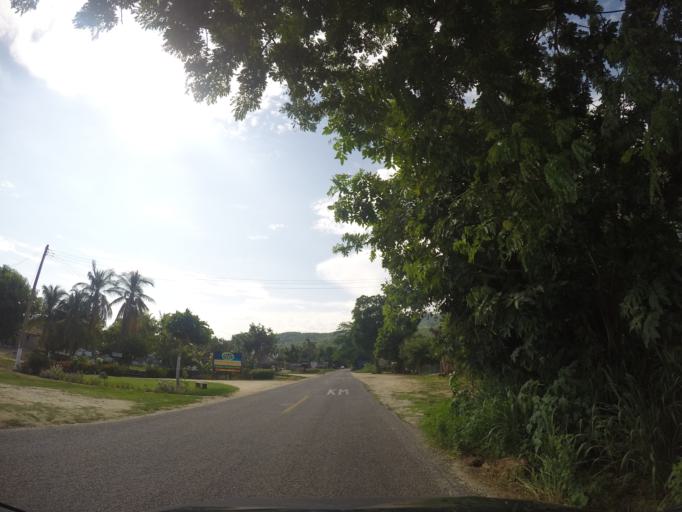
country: MX
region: Oaxaca
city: San Pedro Mixtepec
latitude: 15.9434
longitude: -97.1772
